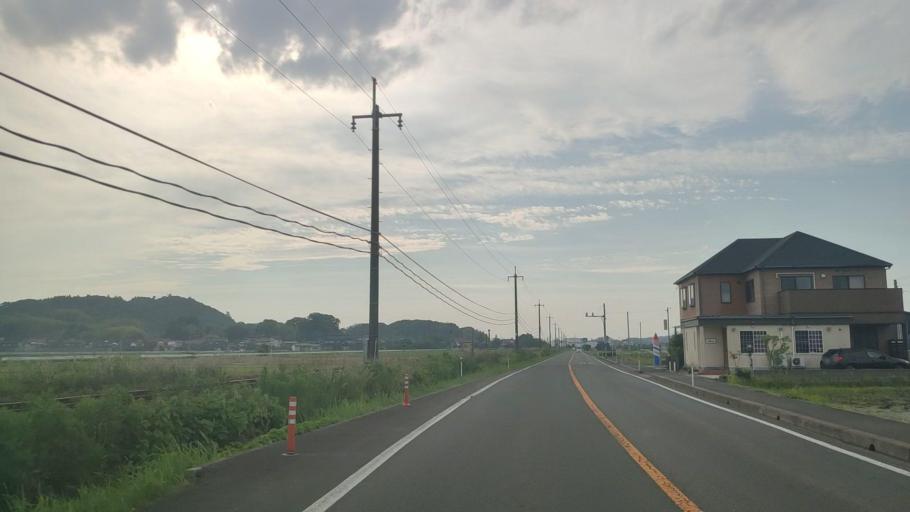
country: JP
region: Tottori
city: Kurayoshi
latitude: 35.4770
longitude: 133.8192
